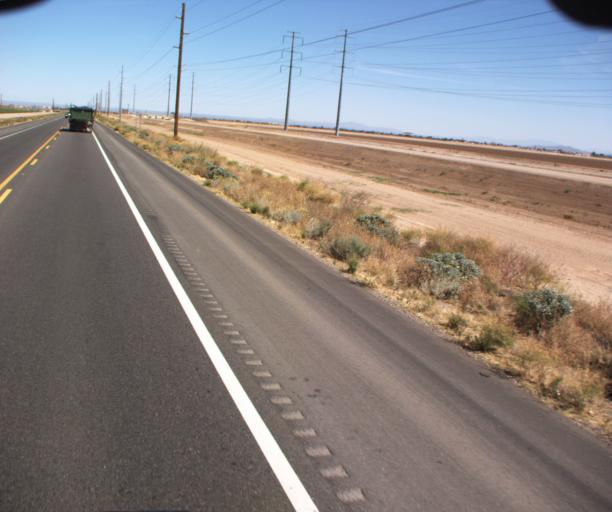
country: US
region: Arizona
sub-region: Pinal County
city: Blackwater
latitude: 33.0024
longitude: -111.5549
